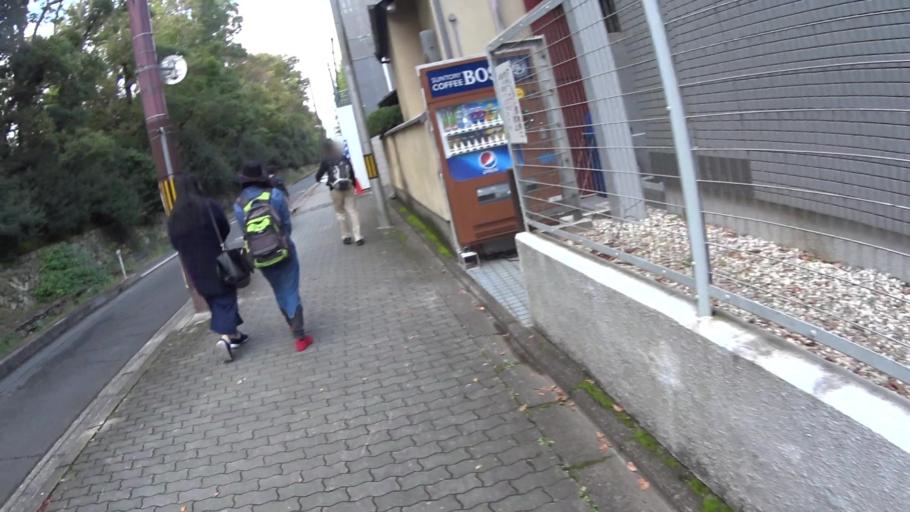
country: JP
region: Kyoto
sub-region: Kyoto-shi
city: Kamigyo-ku
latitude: 35.0260
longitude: 135.7671
